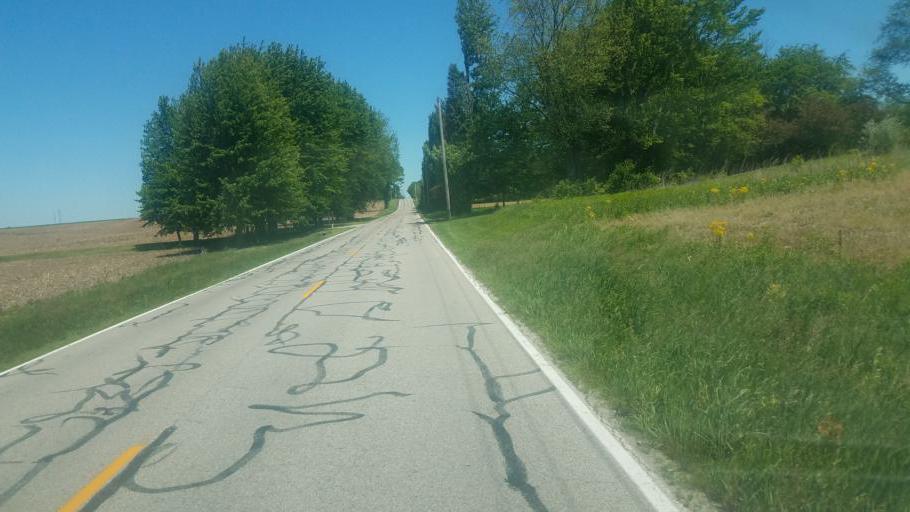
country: US
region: Ohio
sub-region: Shelby County
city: Sidney
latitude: 40.2145
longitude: -84.1682
